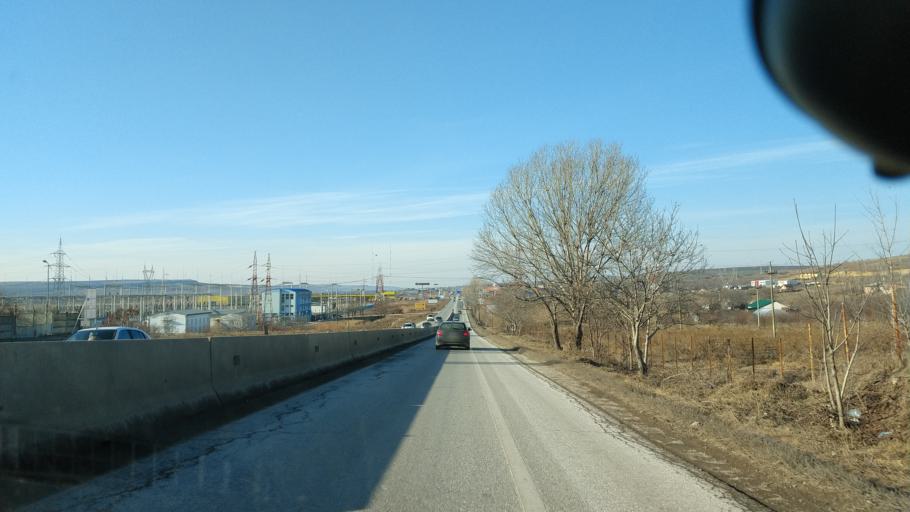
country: RO
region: Iasi
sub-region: Comuna Valea Lupului
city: Valea Lupului
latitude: 47.1782
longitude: 27.4854
